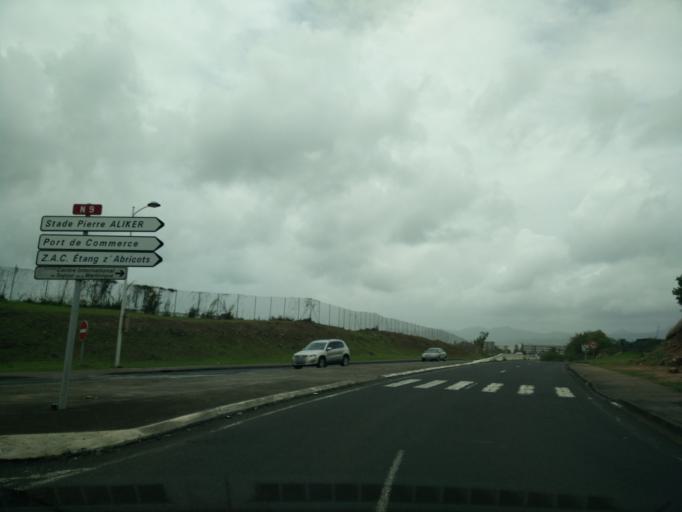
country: MQ
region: Martinique
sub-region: Martinique
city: Fort-de-France
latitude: 14.6114
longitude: -61.0427
